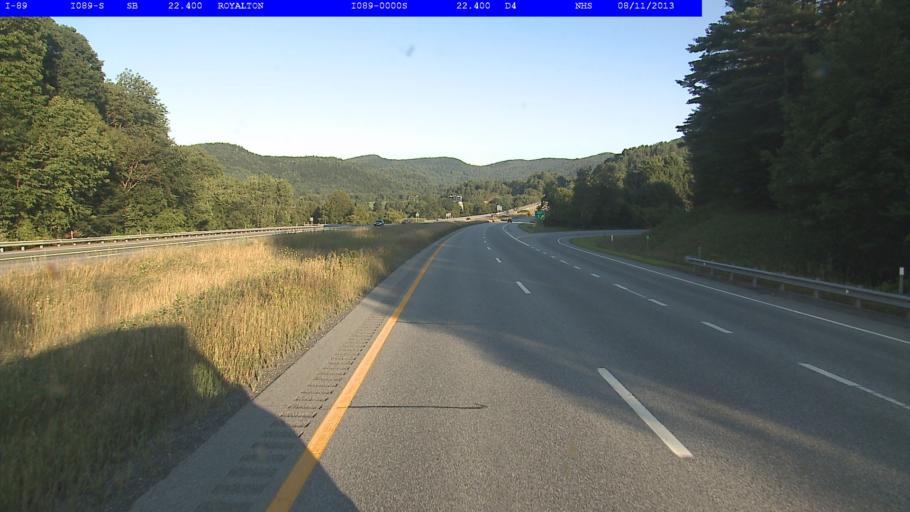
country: US
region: Vermont
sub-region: Orange County
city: Randolph
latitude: 43.8295
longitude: -72.5834
